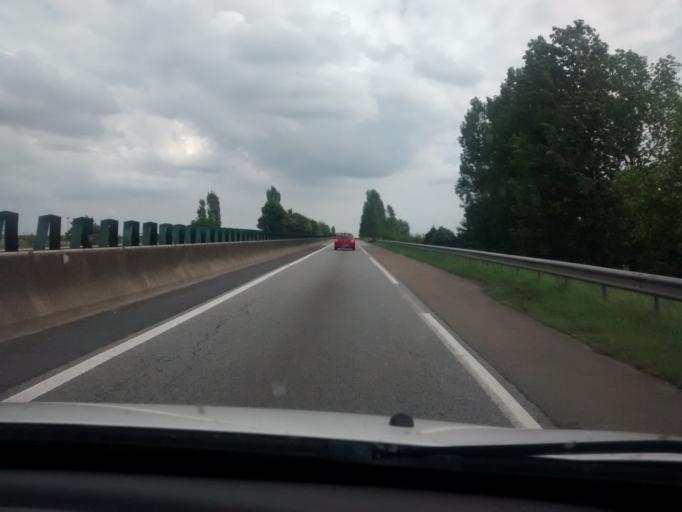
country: FR
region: Ile-de-France
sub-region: Departement des Yvelines
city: Rambouillet
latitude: 48.6564
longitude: 1.8403
